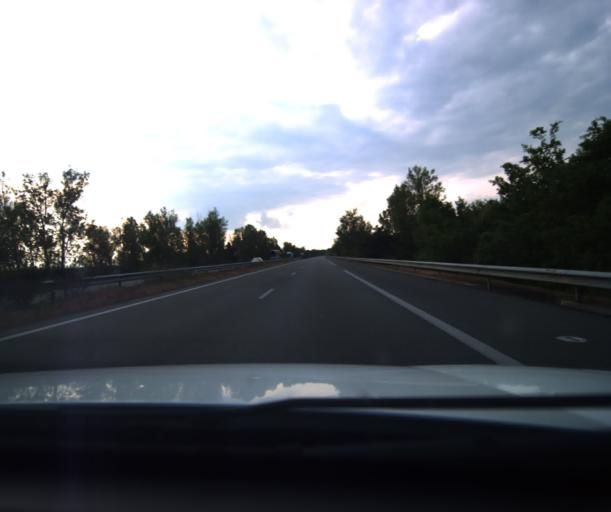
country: FR
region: Midi-Pyrenees
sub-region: Departement du Tarn-et-Garonne
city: Montech
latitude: 43.9832
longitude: 1.2489
